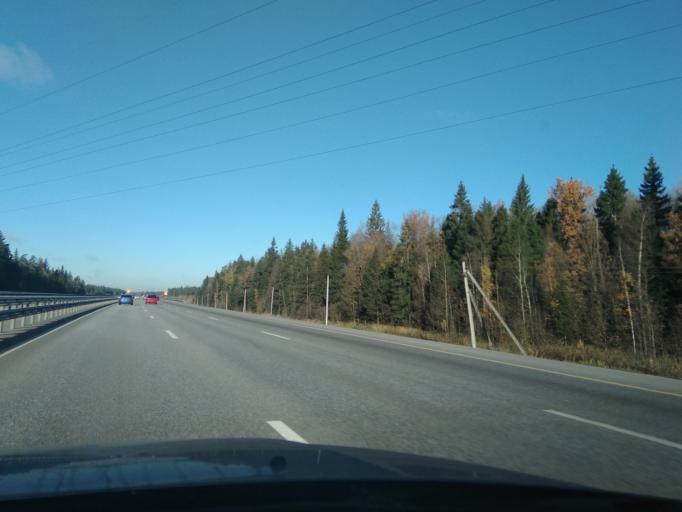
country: RU
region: Moskovskaya
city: Yershovo
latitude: 55.8341
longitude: 36.8483
